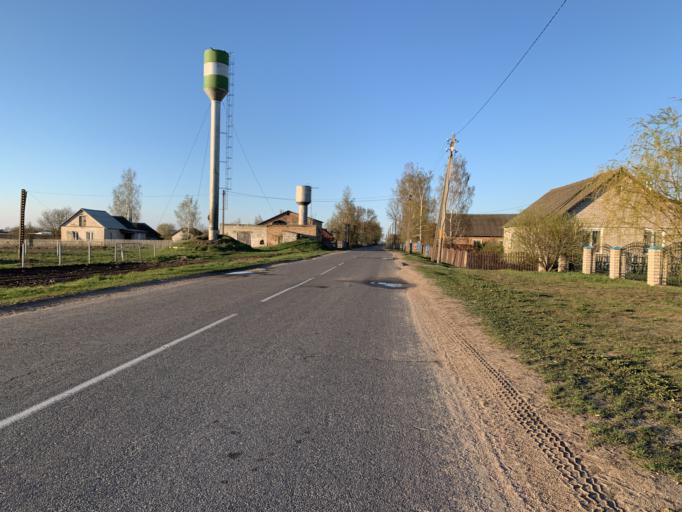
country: BY
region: Minsk
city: Haradzyeya
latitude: 53.3566
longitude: 26.5438
